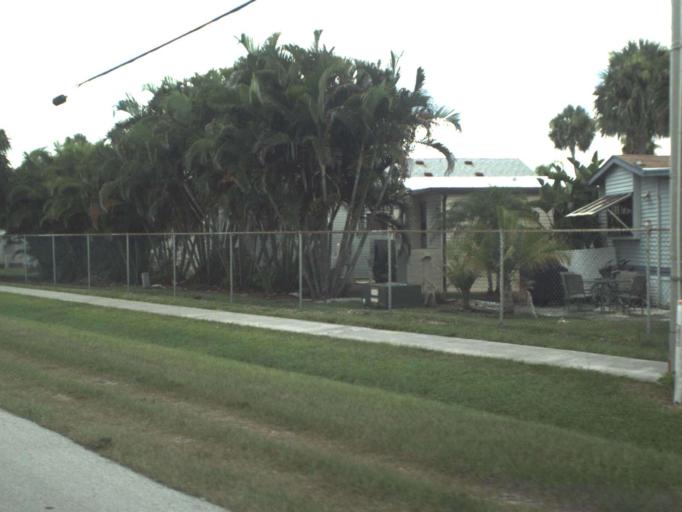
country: US
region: Florida
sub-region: Martin County
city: Jensen Beach
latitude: 27.2700
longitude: -80.2047
